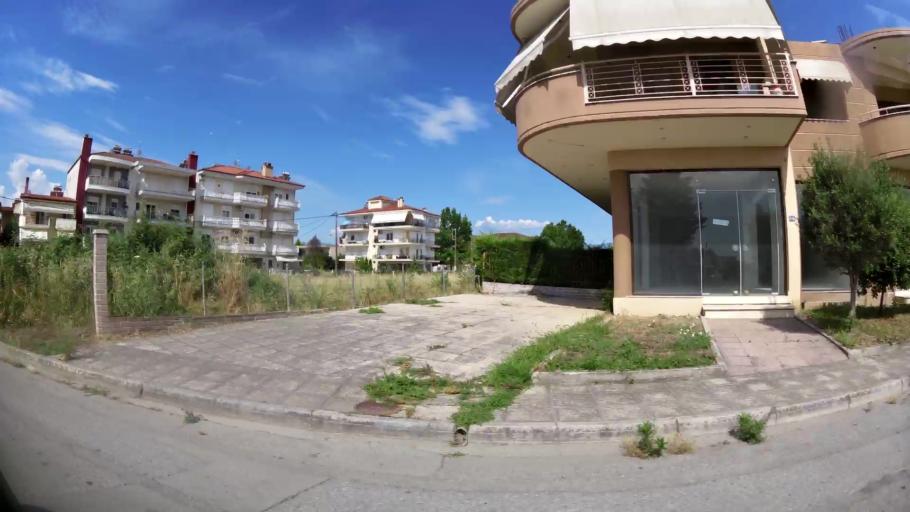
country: GR
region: Central Macedonia
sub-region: Nomos Pierias
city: Katerini
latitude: 40.2848
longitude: 22.5032
